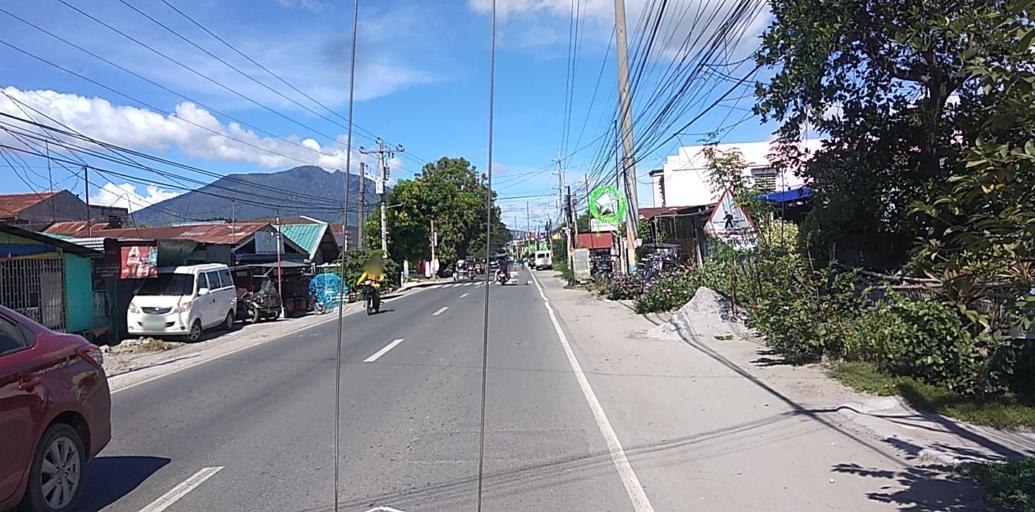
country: PH
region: Central Luzon
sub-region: Province of Pampanga
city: Arayat
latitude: 15.1326
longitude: 120.7746
